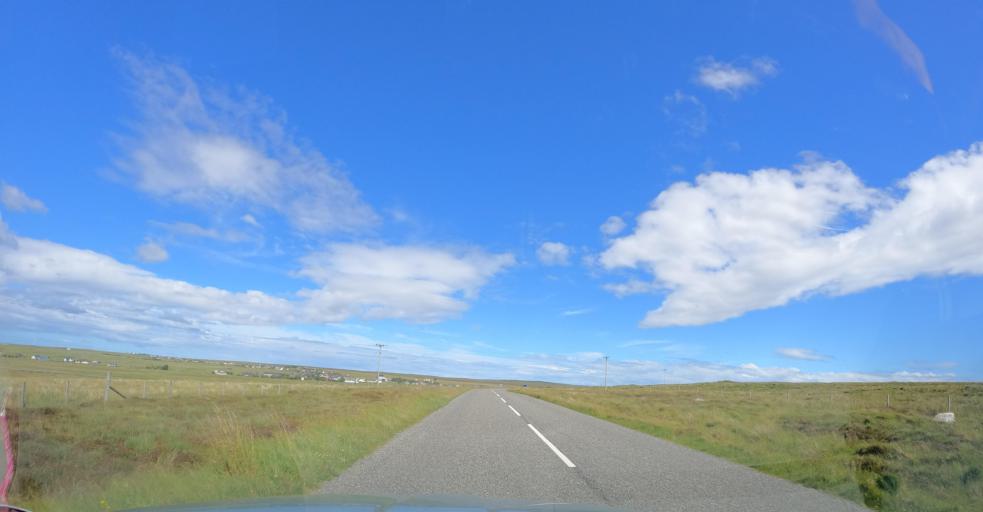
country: GB
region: Scotland
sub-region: Eilean Siar
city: Isle of Lewis
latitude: 58.3493
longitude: -6.5326
